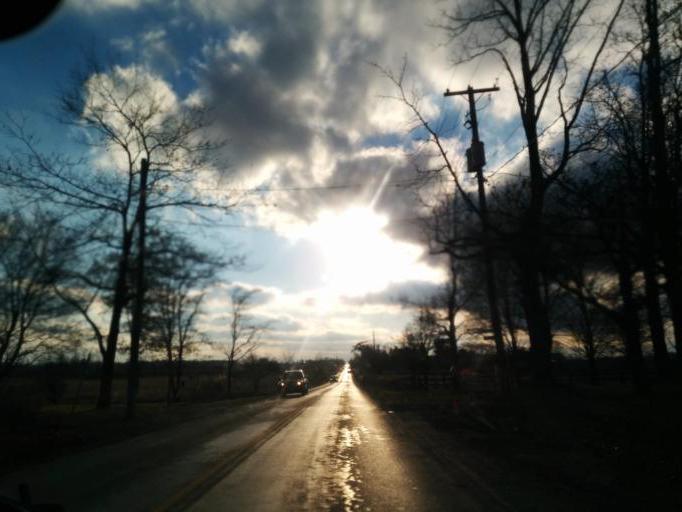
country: CA
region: Ontario
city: Oakville
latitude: 43.5092
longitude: -79.7300
